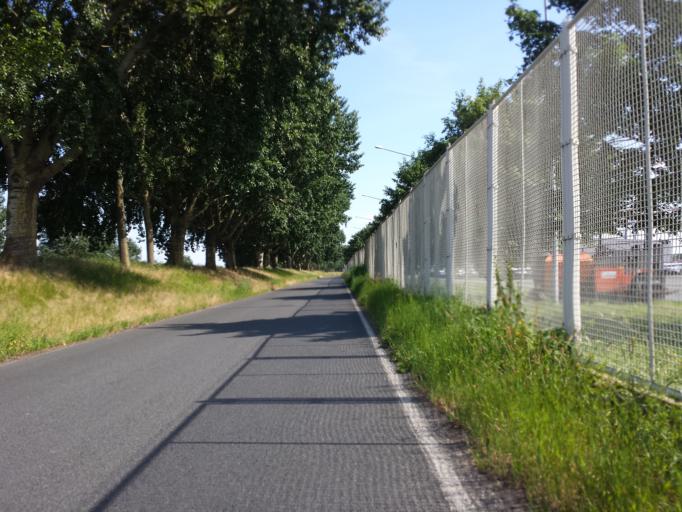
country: DE
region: Bremen
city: Bremen
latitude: 53.1041
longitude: 8.7452
